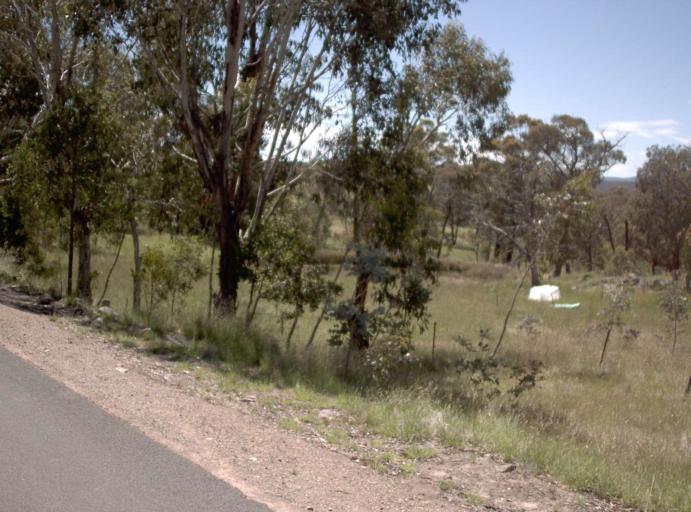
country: AU
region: New South Wales
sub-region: Snowy River
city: Jindabyne
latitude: -37.1115
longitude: 148.2505
